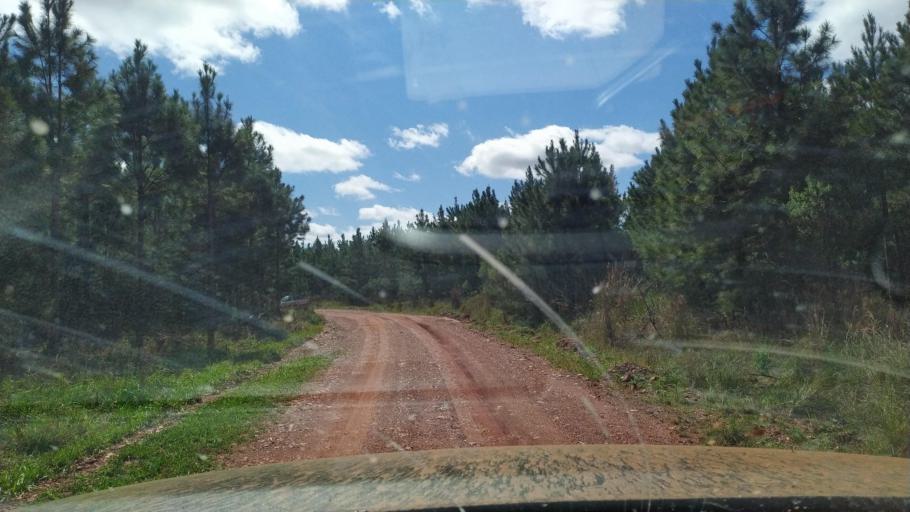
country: AR
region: Corrientes
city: Santo Tome
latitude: -28.4643
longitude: -55.9814
